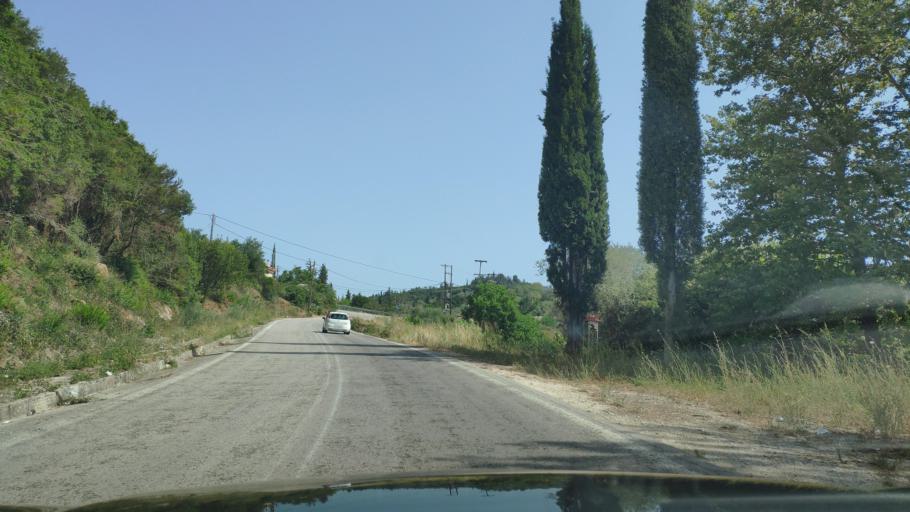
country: GR
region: Epirus
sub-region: Nomos Artas
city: Peta
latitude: 39.1654
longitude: 21.0383
